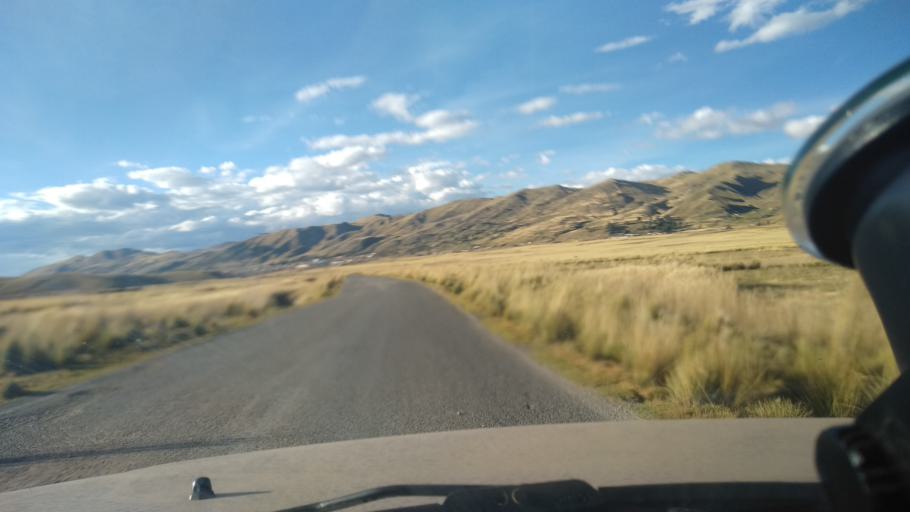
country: PE
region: Cusco
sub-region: Provincia de Canas
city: Chignayhua
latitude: -14.2469
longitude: -71.4345
